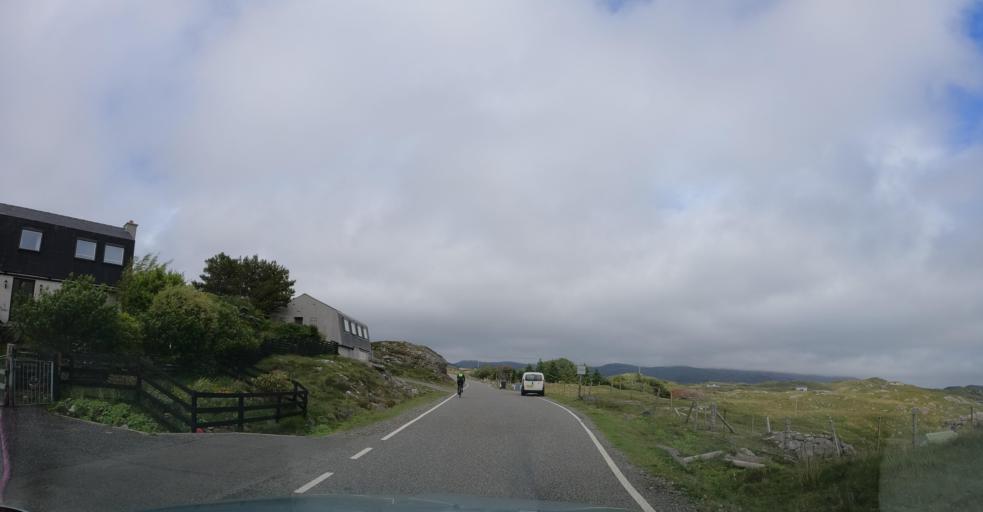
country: GB
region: Scotland
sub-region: Eilean Siar
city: Harris
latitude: 57.8831
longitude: -6.8136
